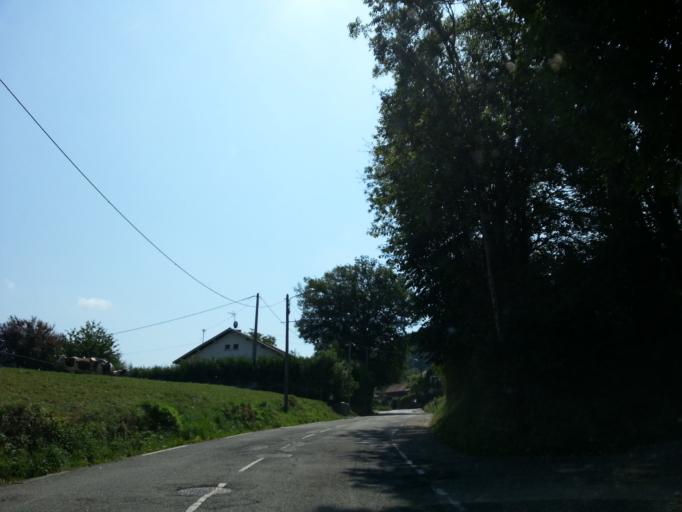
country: FR
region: Rhone-Alpes
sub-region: Departement de la Haute-Savoie
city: Annecy-le-Vieux
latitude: 45.9207
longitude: 6.1725
